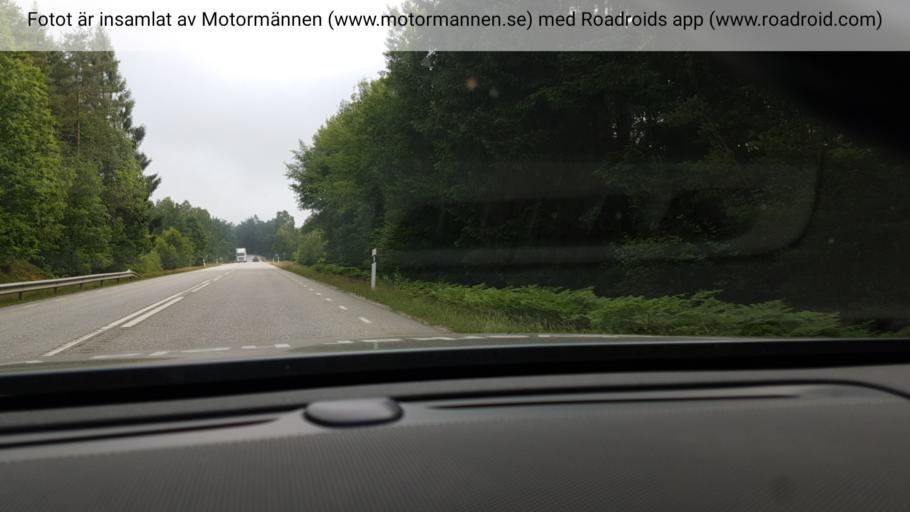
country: SE
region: Skane
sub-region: Hassleholms Kommun
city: Bjarnum
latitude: 56.2621
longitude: 13.7186
